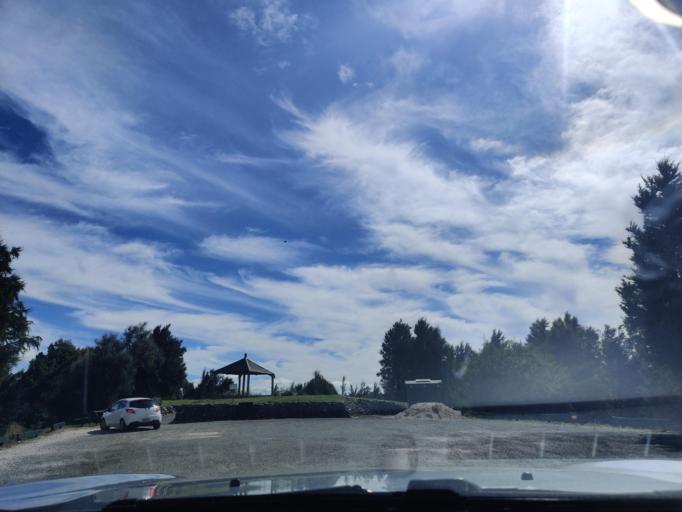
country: NZ
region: Tasman
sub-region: Tasman District
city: Wakefield
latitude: -41.6280
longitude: 172.7196
